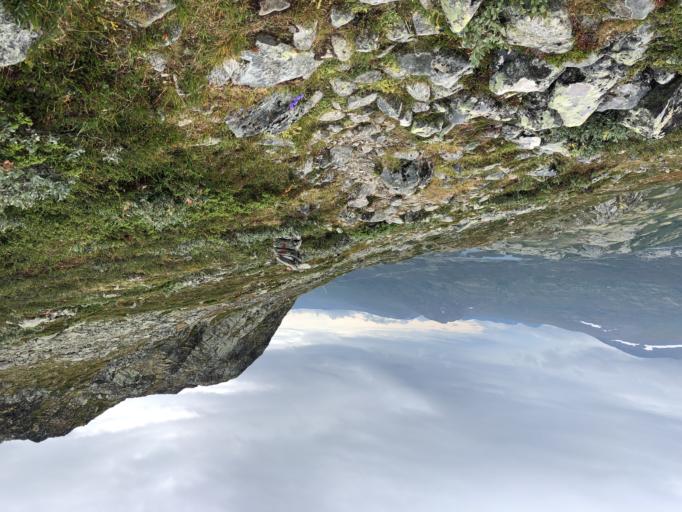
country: NO
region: Oppland
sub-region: Lom
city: Fossbergom
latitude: 61.5163
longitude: 8.8147
